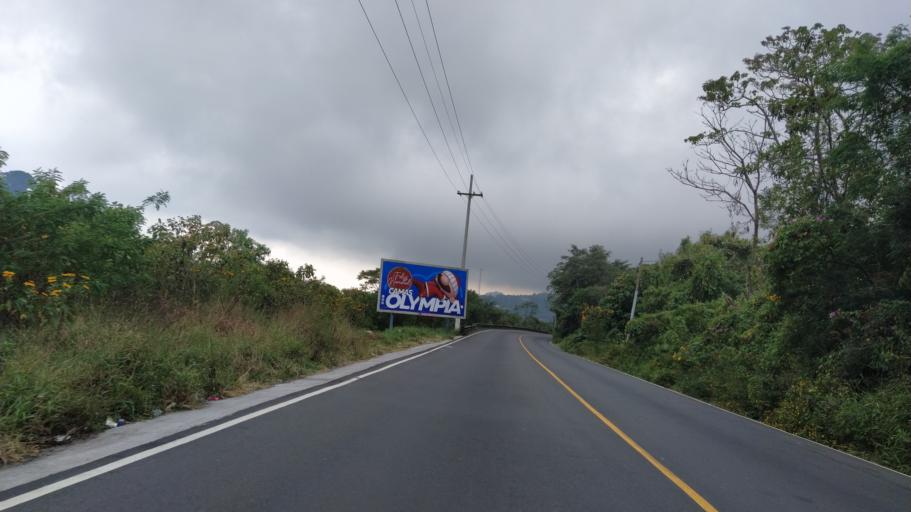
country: GT
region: Quetzaltenango
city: Zunil
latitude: 14.7314
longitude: -91.5210
